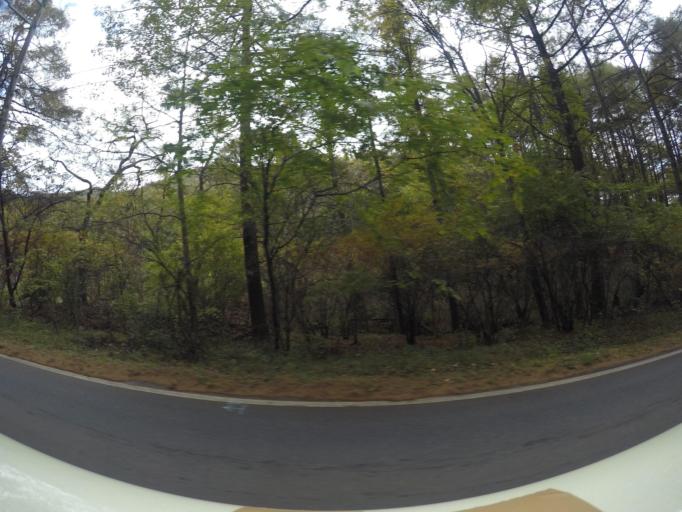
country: JP
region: Nagano
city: Chino
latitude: 35.9659
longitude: 138.1187
